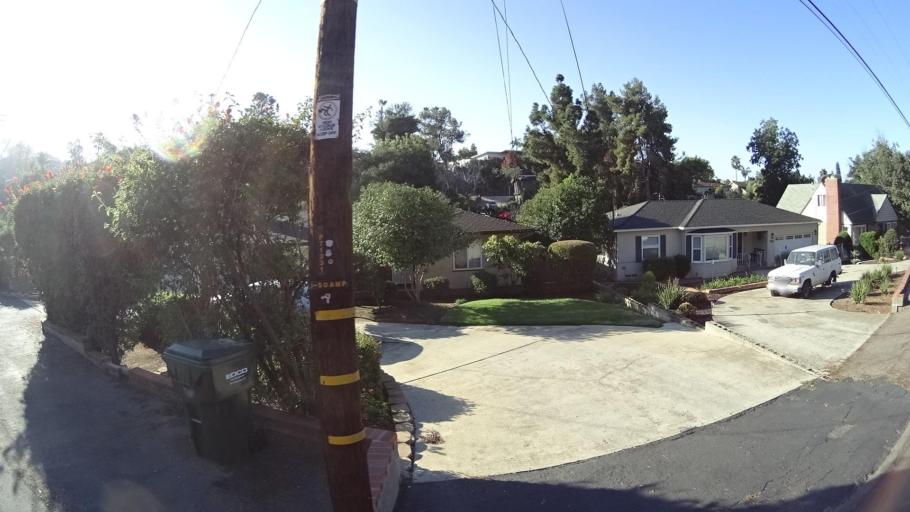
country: US
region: California
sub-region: San Diego County
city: La Mesa
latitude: 32.7762
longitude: -116.9976
